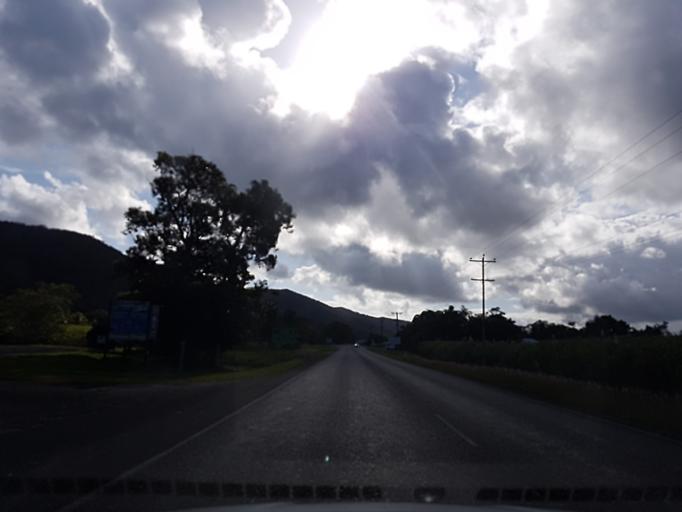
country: AU
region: Queensland
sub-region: Cairns
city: Port Douglas
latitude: -16.2857
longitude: 145.3811
